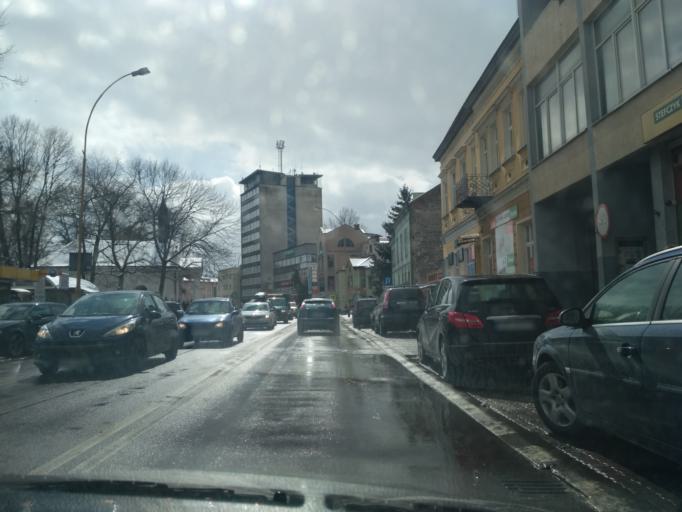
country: PL
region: Subcarpathian Voivodeship
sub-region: Rzeszow
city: Rzeszow
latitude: 50.0383
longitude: 22.0099
